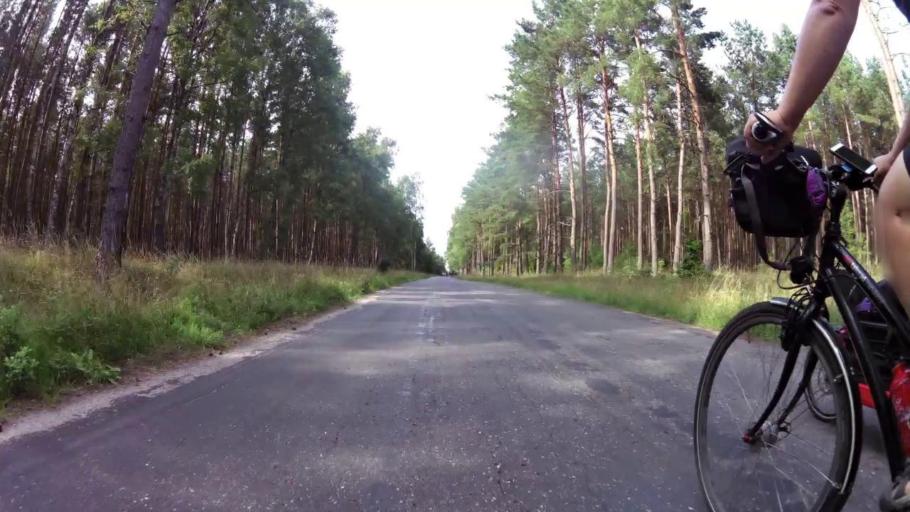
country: PL
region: West Pomeranian Voivodeship
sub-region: Powiat stargardzki
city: Insko
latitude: 53.3838
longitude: 15.5966
